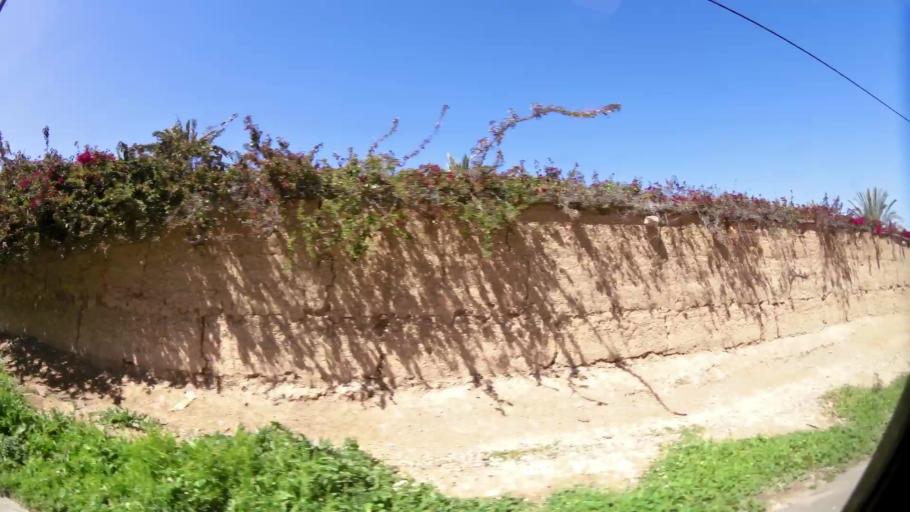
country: MA
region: Marrakech-Tensift-Al Haouz
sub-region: Marrakech
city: Marrakesh
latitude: 31.6700
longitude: -7.9789
